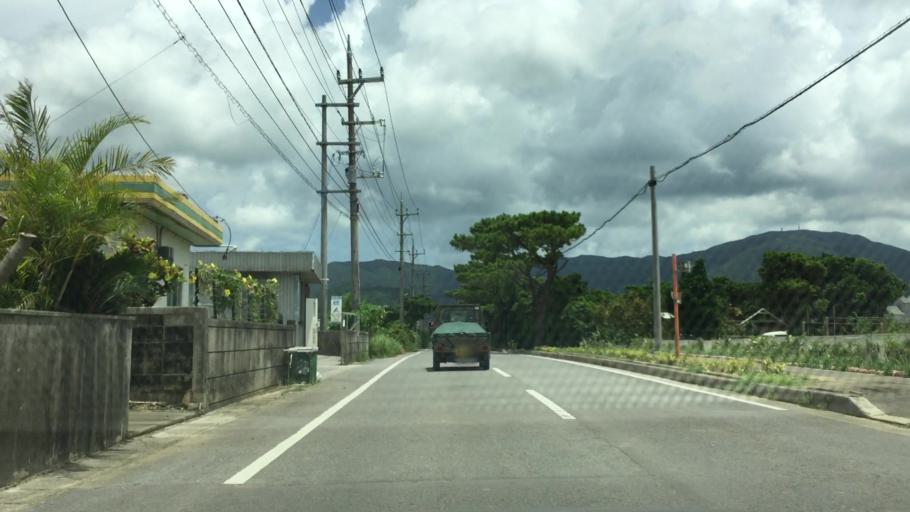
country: JP
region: Okinawa
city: Ishigaki
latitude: 24.3908
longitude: 124.1550
